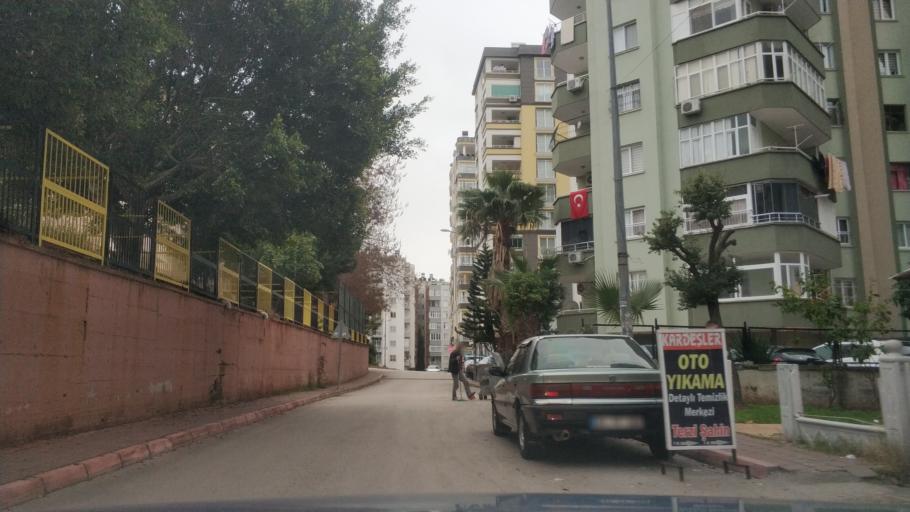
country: TR
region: Adana
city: Seyhan
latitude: 37.0546
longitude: 35.2795
